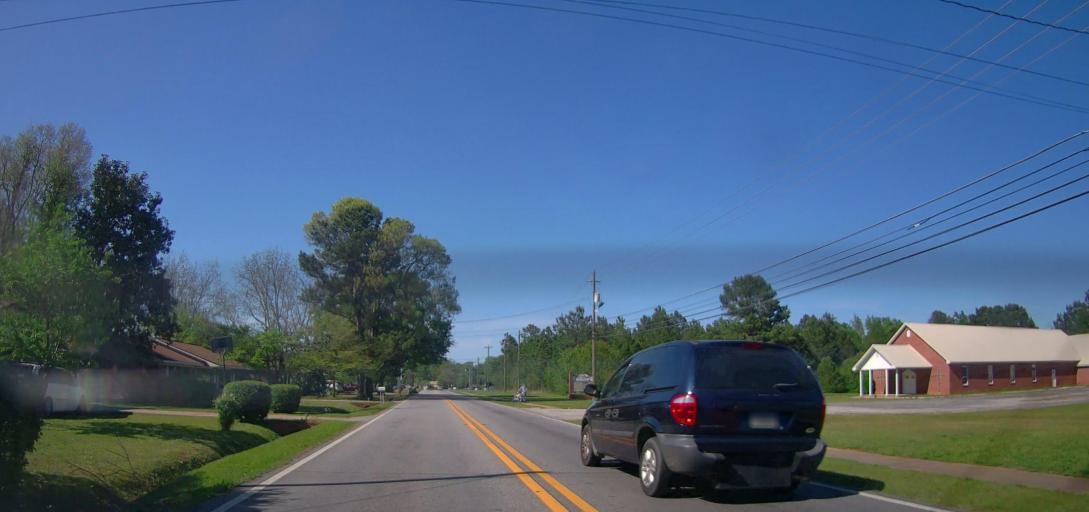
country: US
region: Georgia
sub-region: Houston County
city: Warner Robins
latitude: 32.6365
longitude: -83.6321
